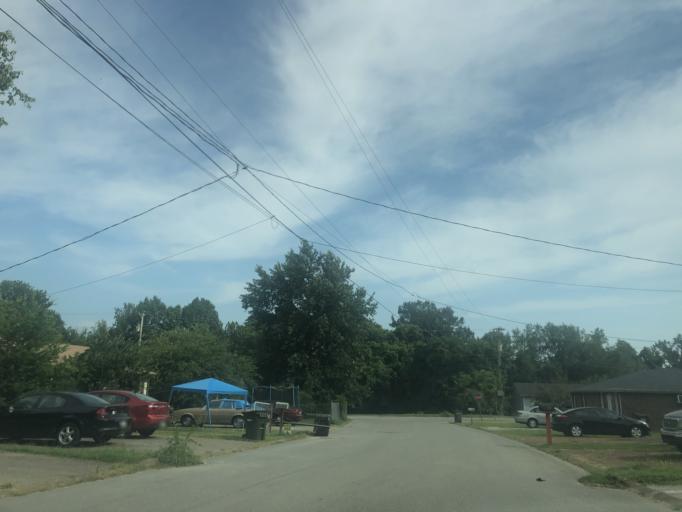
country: US
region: Tennessee
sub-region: Wilson County
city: Green Hill
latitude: 36.1751
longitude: -86.5876
